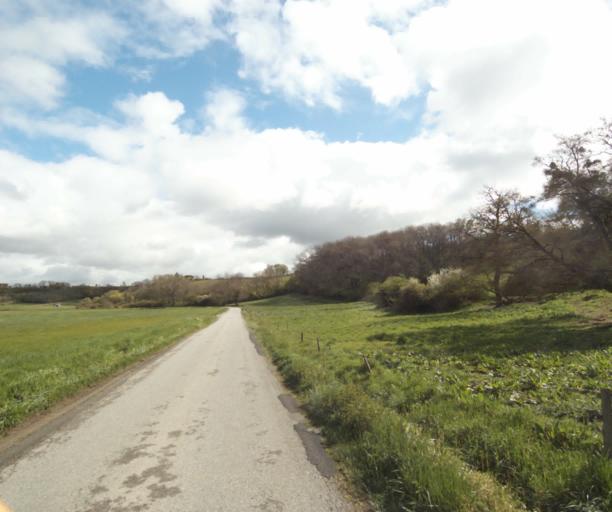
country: FR
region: Midi-Pyrenees
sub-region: Departement de l'Ariege
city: Saverdun
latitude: 43.2282
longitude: 1.5615
